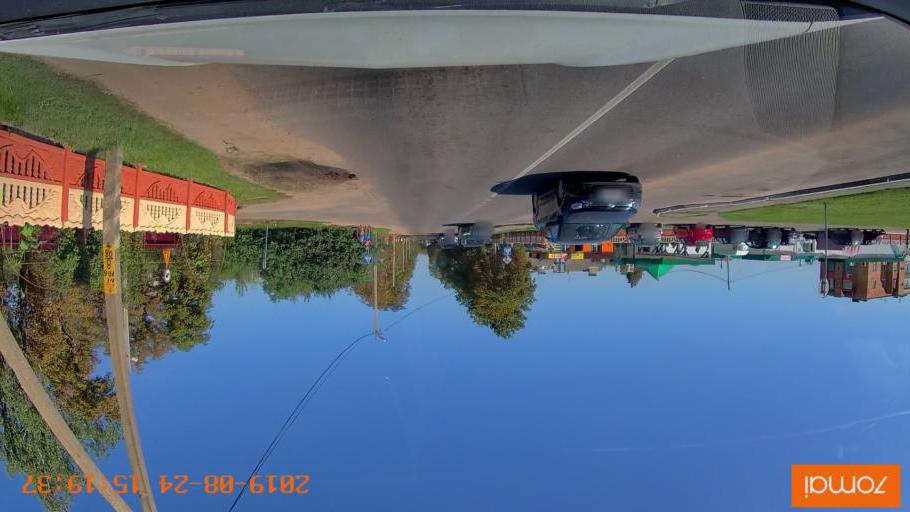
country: BY
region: Minsk
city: Samakhvalavichy
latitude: 53.6762
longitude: 27.5308
